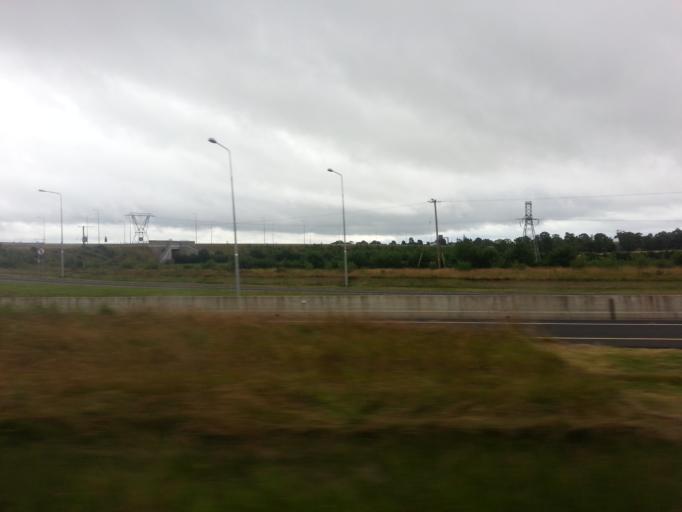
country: IE
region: Leinster
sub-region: Kilkenny
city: Kilkenny
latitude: 52.6347
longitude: -7.1492
